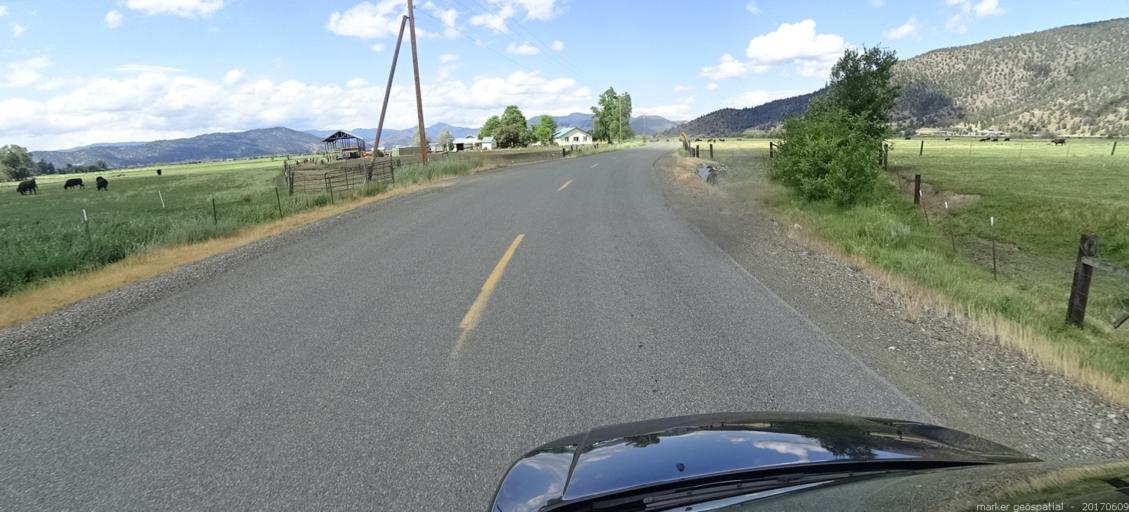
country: US
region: California
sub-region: Siskiyou County
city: Yreka
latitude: 41.5085
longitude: -122.8564
